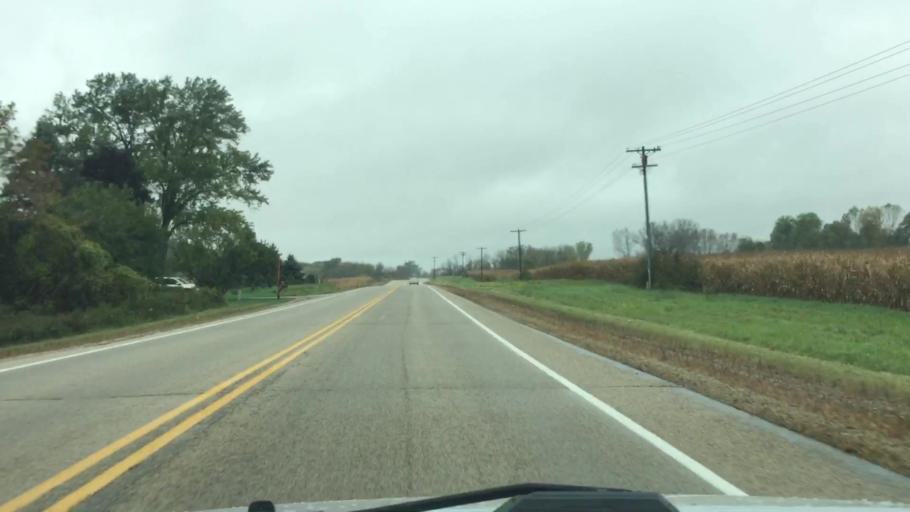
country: US
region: Wisconsin
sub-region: Jefferson County
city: Palmyra
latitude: 42.8789
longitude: -88.6119
